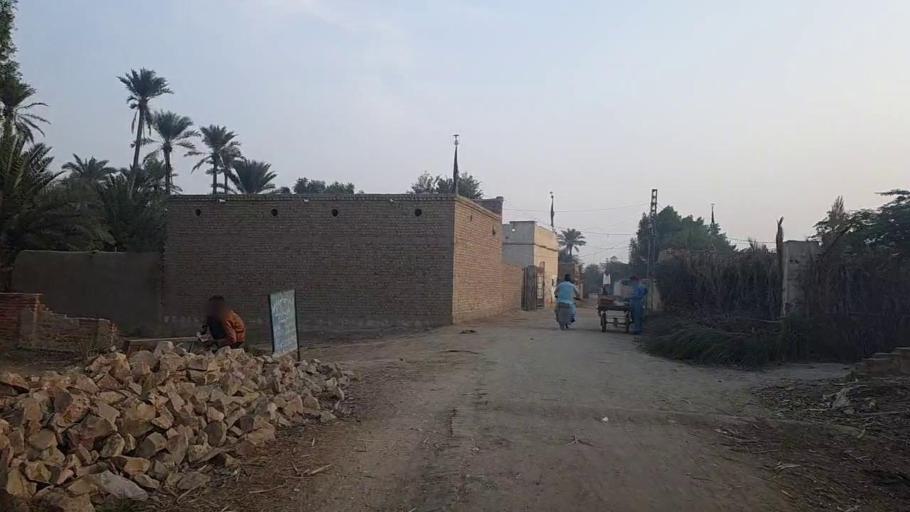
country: PK
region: Sindh
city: Kot Diji
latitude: 27.3788
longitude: 68.6652
